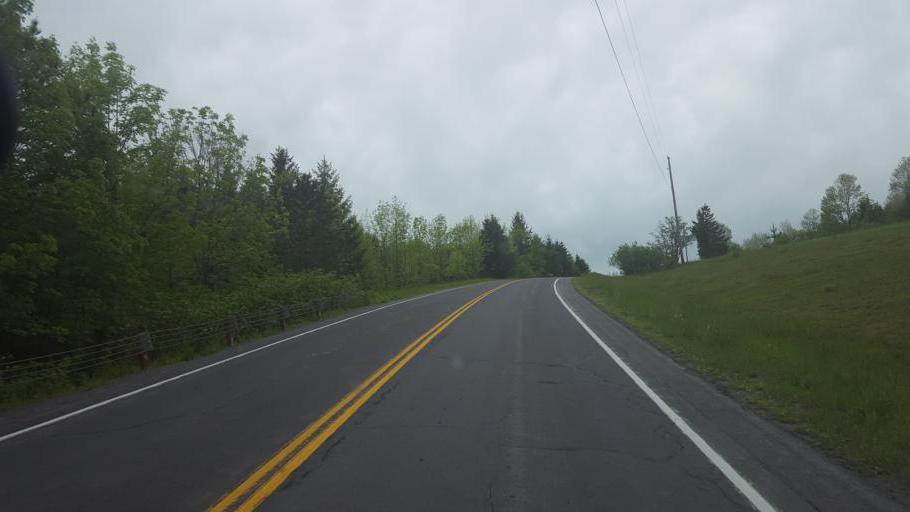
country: US
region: New York
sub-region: Herkimer County
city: Ilion
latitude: 42.9324
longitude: -75.0563
